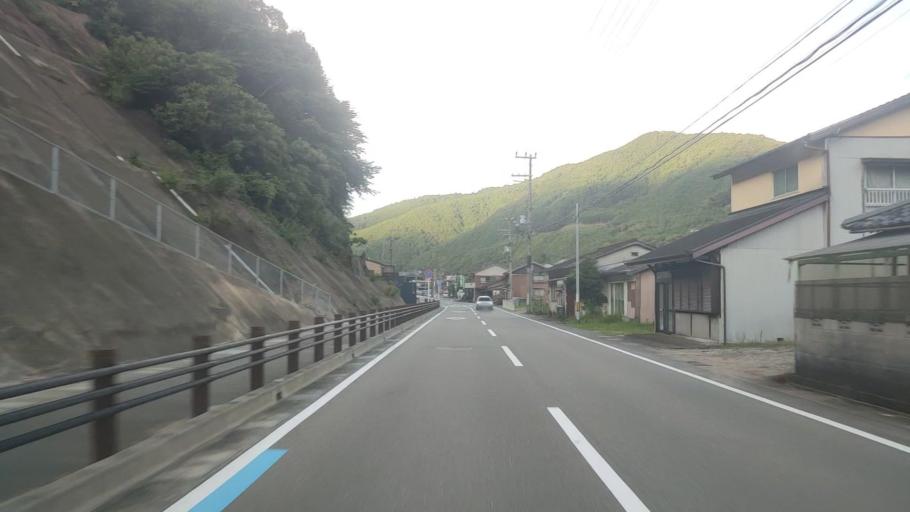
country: JP
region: Wakayama
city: Tanabe
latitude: 33.7882
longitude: 135.5135
